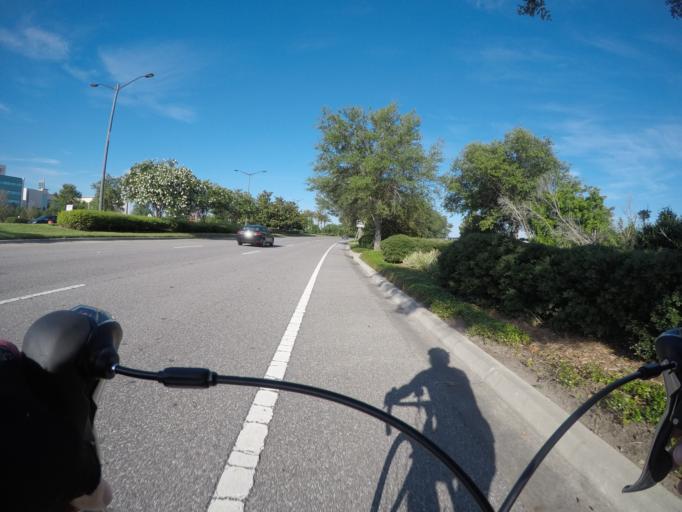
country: US
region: Florida
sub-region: Osceola County
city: Buenaventura Lakes
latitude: 28.3701
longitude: -81.2800
